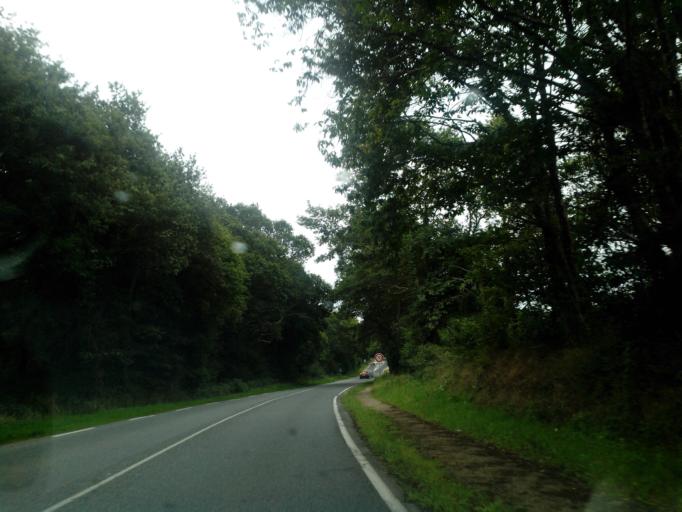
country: FR
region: Brittany
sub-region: Departement du Finistere
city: Quimperle
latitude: 47.8624
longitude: -3.5203
